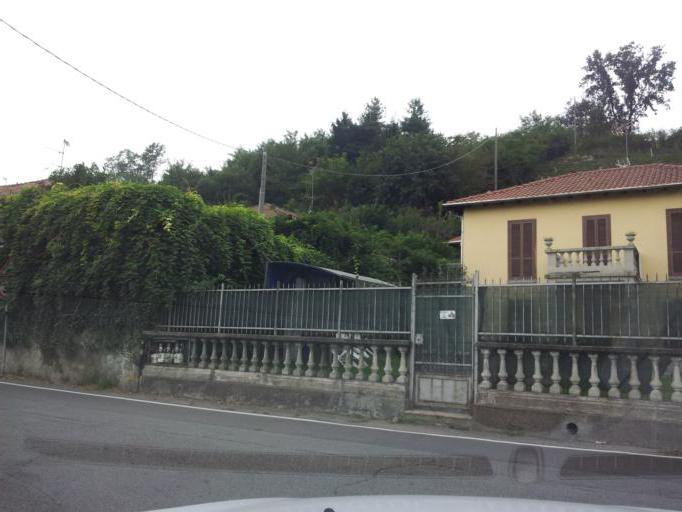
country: IT
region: Lombardy
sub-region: Provincia di Varese
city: Mercallo
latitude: 45.7355
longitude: 8.6631
